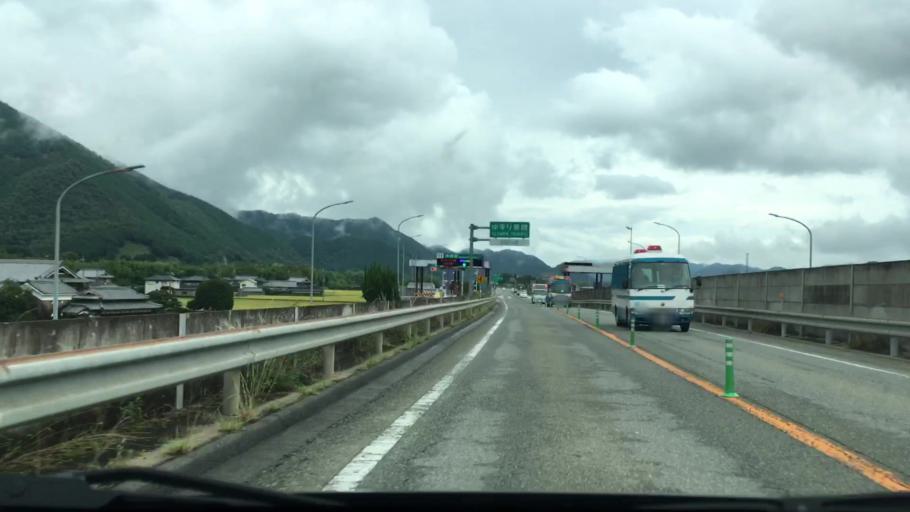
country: JP
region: Hyogo
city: Yamazakicho-nakabirose
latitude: 35.0568
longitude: 134.7637
